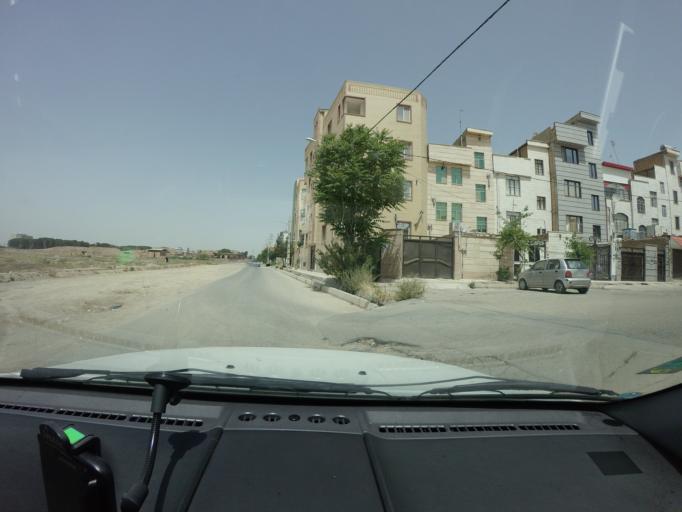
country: IR
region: Tehran
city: Eslamshahr
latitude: 35.5254
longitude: 51.2206
